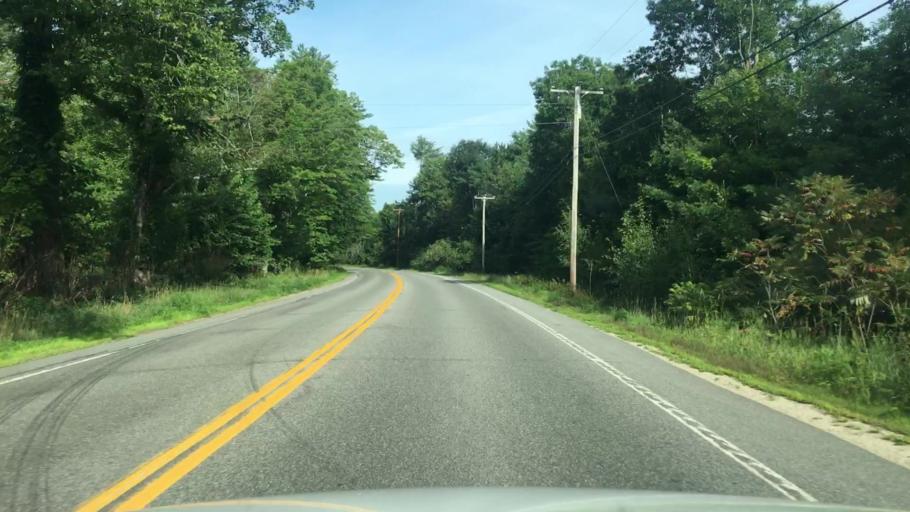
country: US
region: Maine
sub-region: York County
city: Cornish
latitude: 43.8054
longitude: -70.8354
